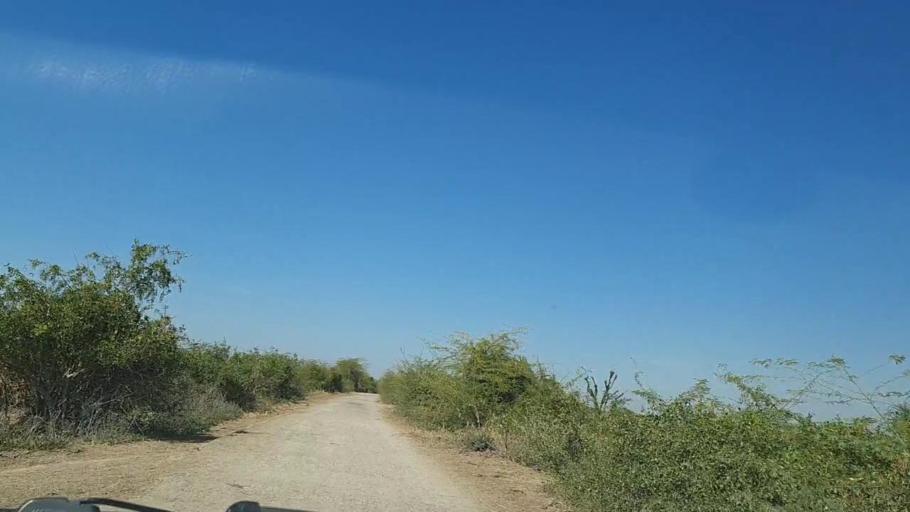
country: PK
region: Sindh
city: Dhoro Naro
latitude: 25.5372
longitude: 69.5005
